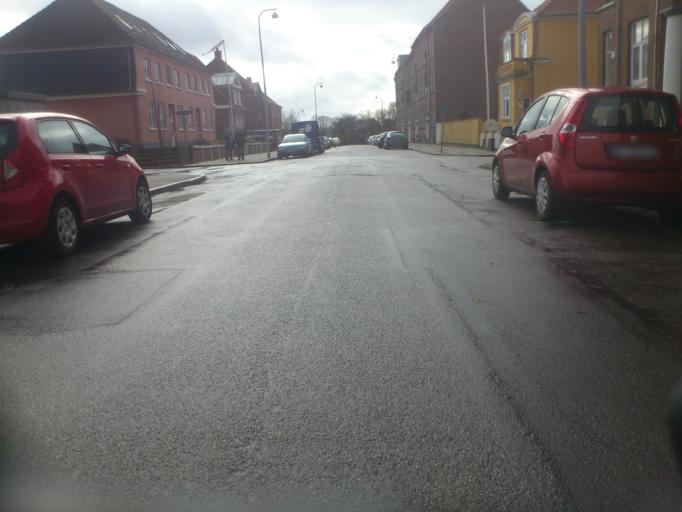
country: DK
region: South Denmark
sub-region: Fredericia Kommune
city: Fredericia
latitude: 55.5613
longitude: 9.7656
